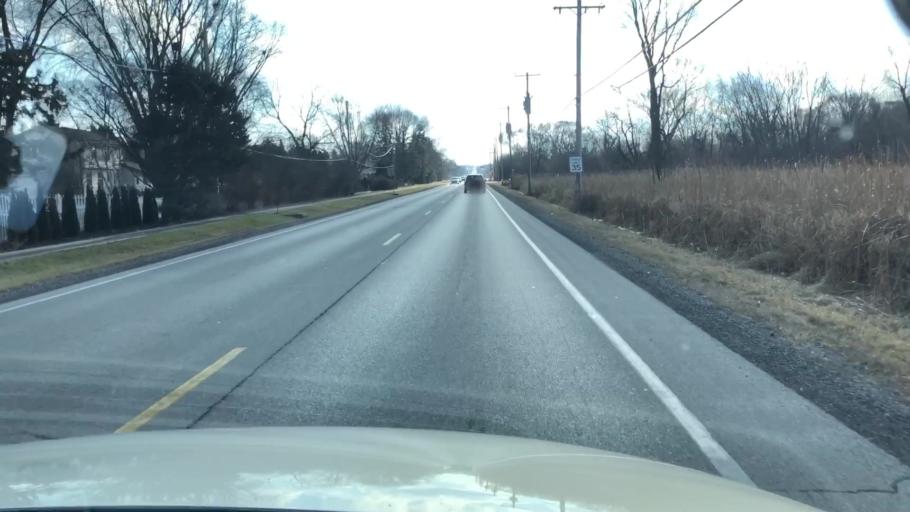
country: US
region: Wisconsin
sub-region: Waukesha County
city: Waukesha
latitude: 43.0612
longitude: -88.1859
